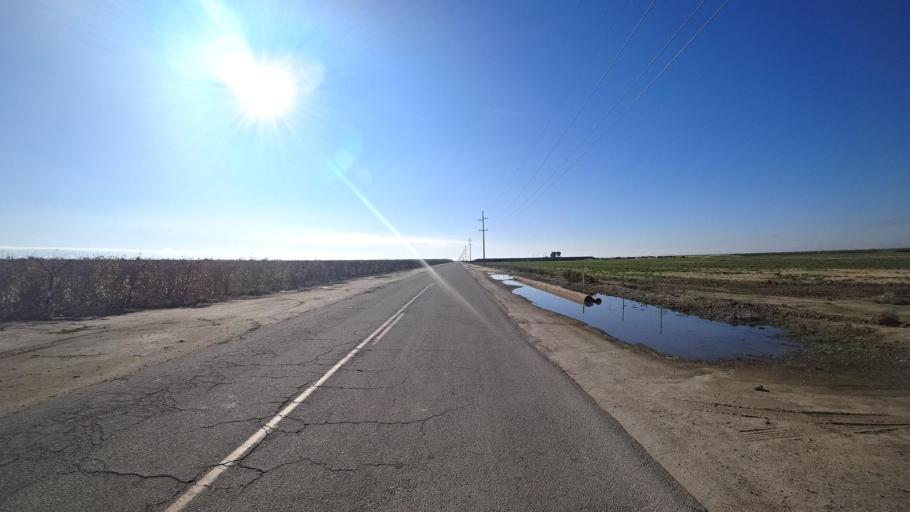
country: US
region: California
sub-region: Kern County
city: McFarland
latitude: 35.6882
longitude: -119.2764
